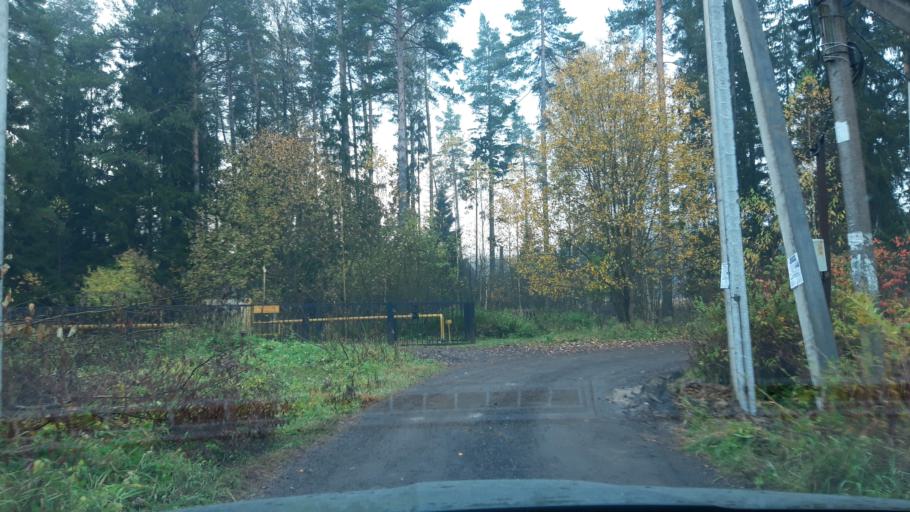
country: RU
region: Moskovskaya
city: Lozhki
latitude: 56.0492
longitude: 37.0991
